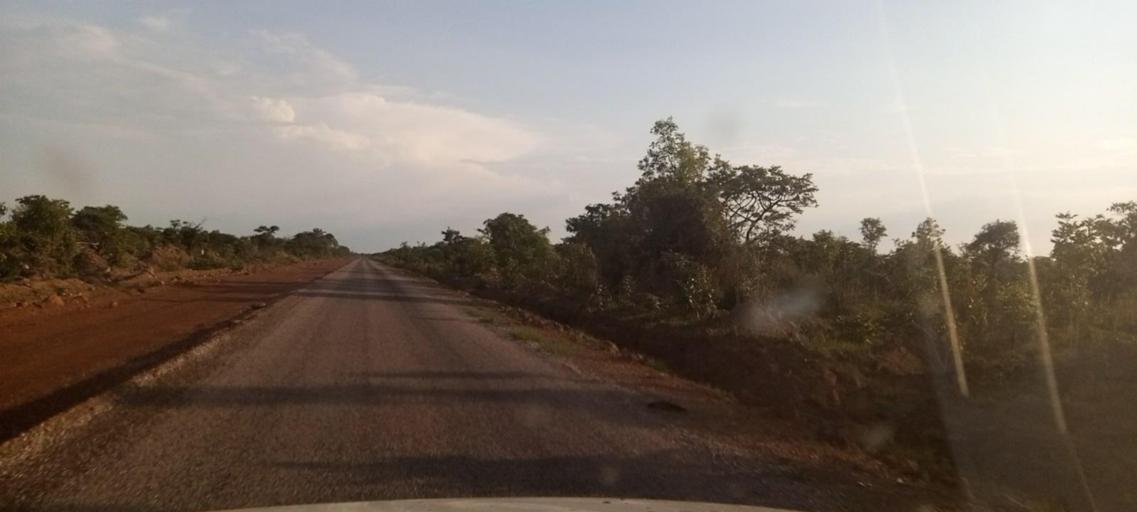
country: CD
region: Katanga
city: Kambove
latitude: -10.0428
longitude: 26.9469
